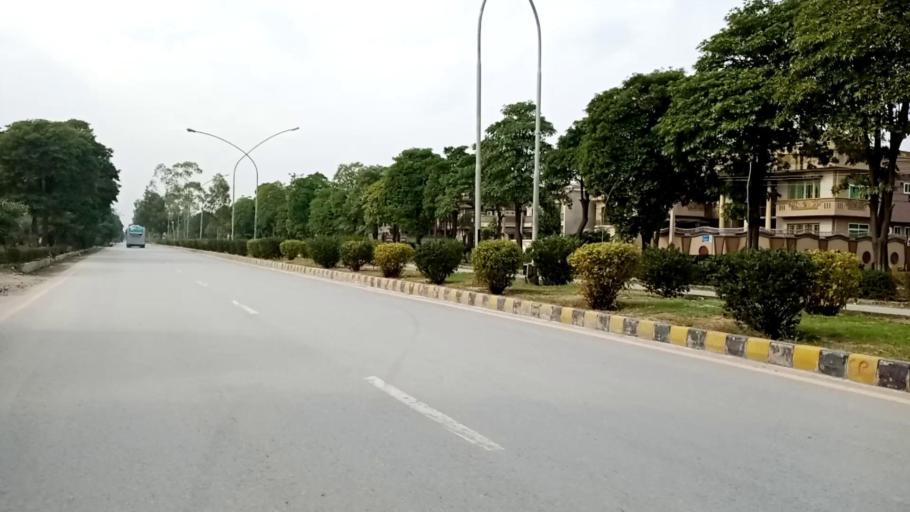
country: PK
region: Khyber Pakhtunkhwa
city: Peshawar
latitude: 33.9563
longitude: 71.4415
